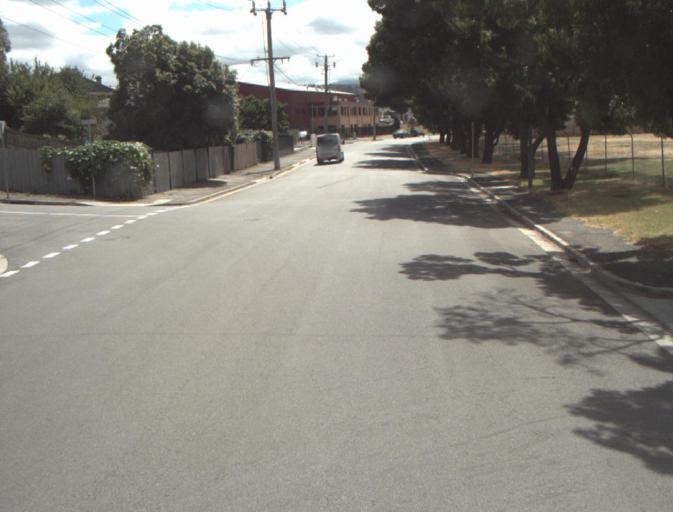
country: AU
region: Tasmania
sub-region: Launceston
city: Launceston
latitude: -41.4223
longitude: 147.1400
